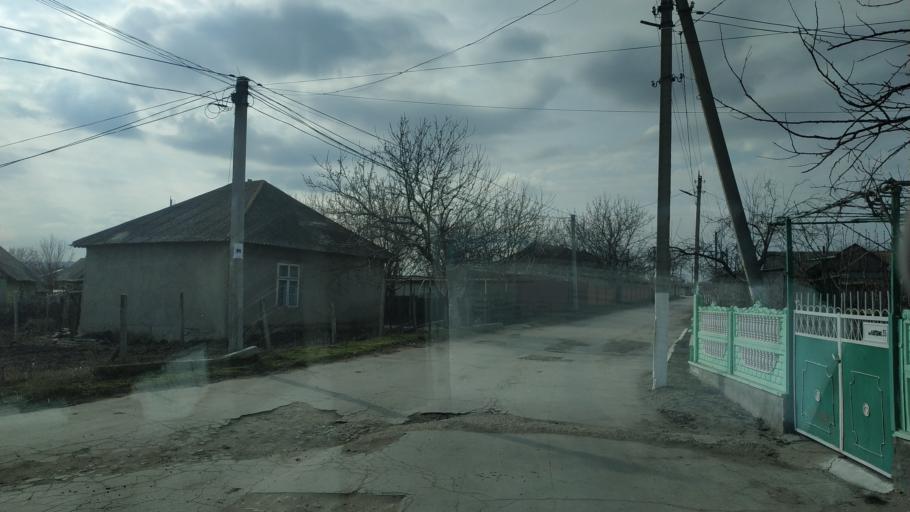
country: MD
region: Anenii Noi
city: Anenii Noi
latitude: 46.9060
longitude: 29.1433
